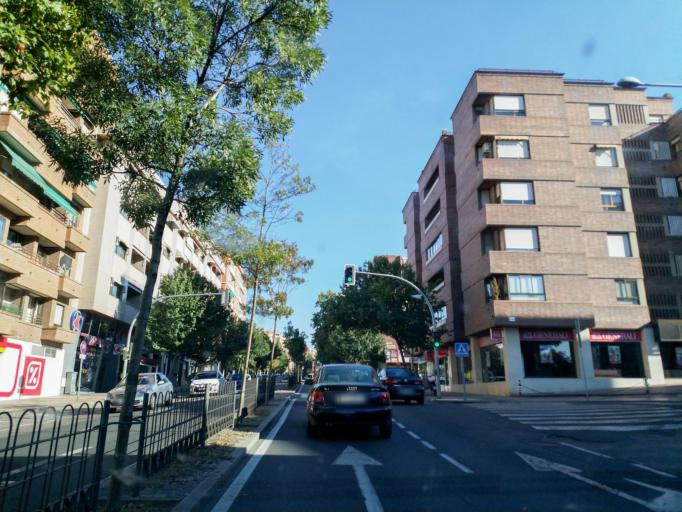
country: ES
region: Castille and Leon
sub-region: Provincia de Segovia
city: Segovia
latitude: 40.9436
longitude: -4.1201
